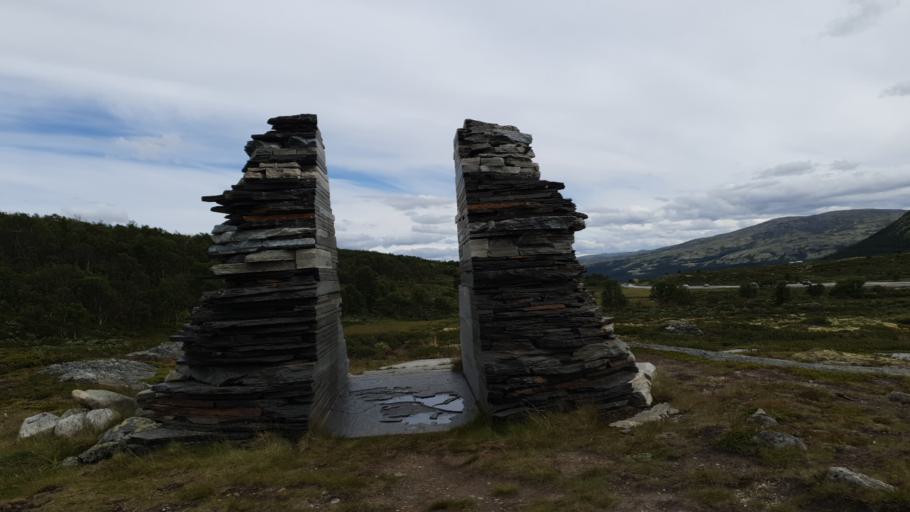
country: NO
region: Oppland
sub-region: Dovre
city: Dovre
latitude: 62.2324
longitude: 9.5340
